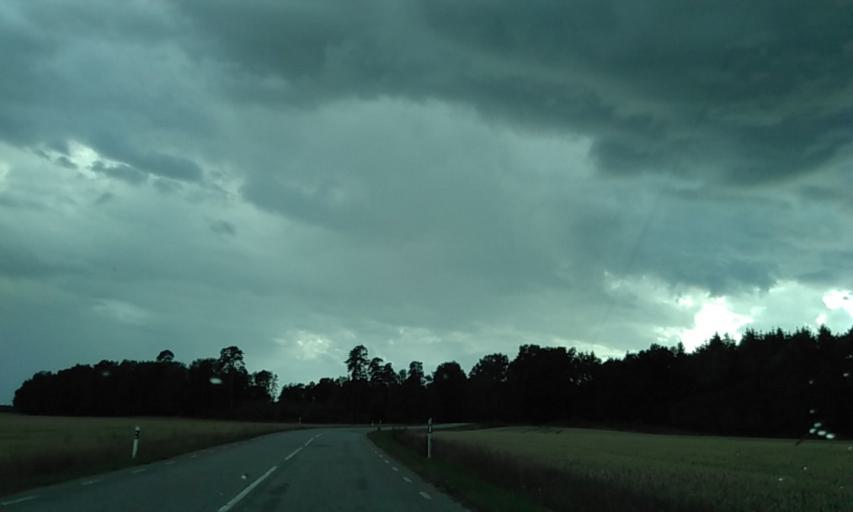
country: SE
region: Vaestra Goetaland
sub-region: Grastorps Kommun
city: Graestorp
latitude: 58.4772
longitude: 12.8365
